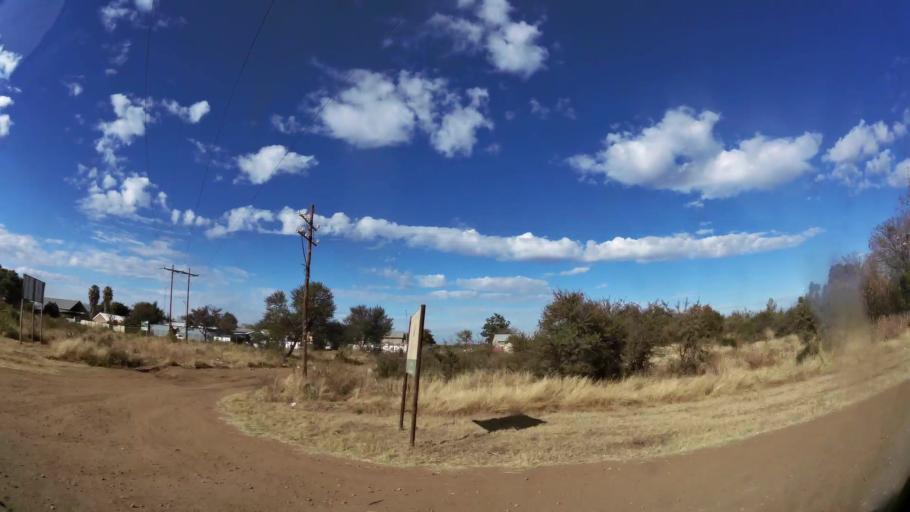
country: ZA
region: Limpopo
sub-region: Waterberg District Municipality
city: Bela-Bela
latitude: -24.8915
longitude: 28.3003
